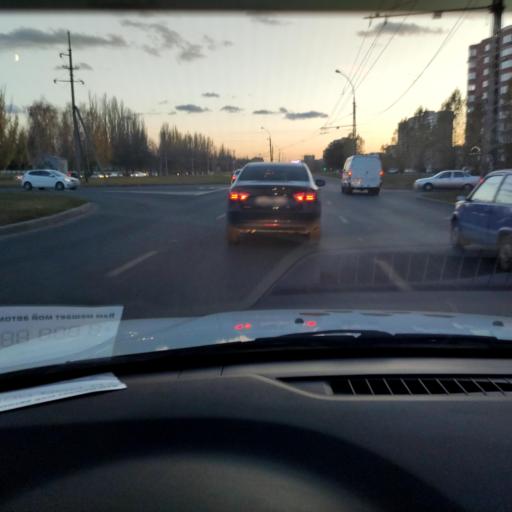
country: RU
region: Samara
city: Tol'yatti
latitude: 53.5156
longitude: 49.3078
